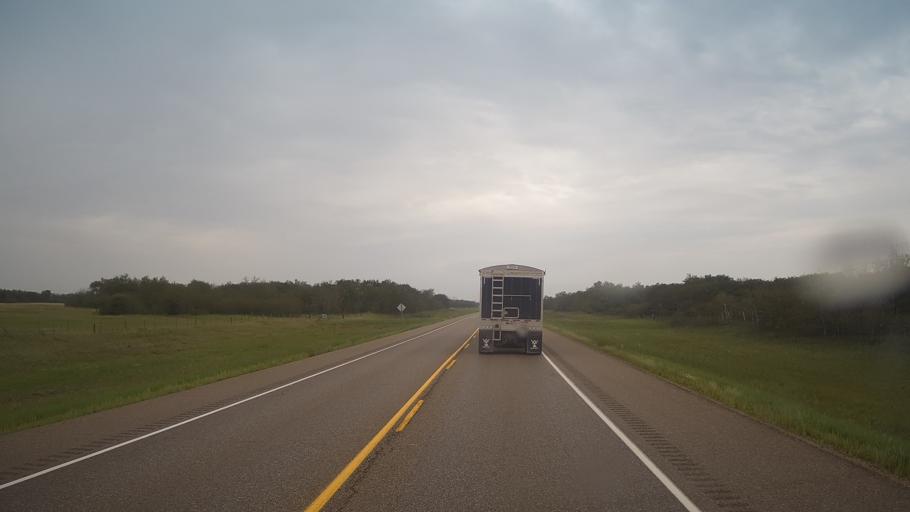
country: CA
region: Saskatchewan
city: Langham
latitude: 52.1294
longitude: -107.0519
